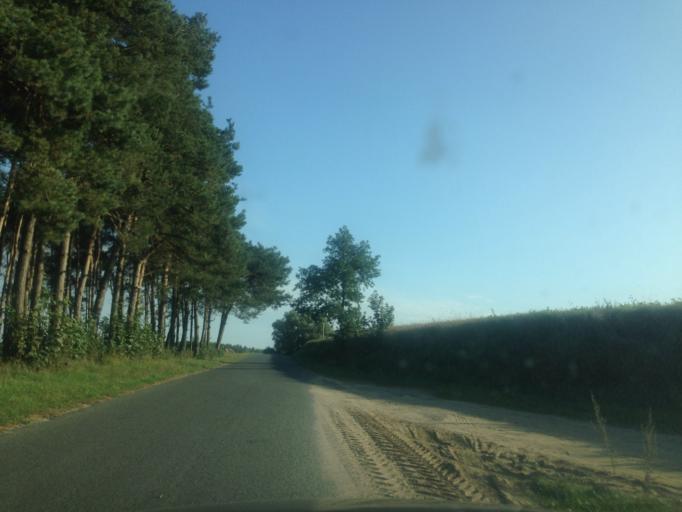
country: PL
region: Kujawsko-Pomorskie
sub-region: Powiat brodnicki
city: Brzozie
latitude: 53.2934
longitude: 19.6904
